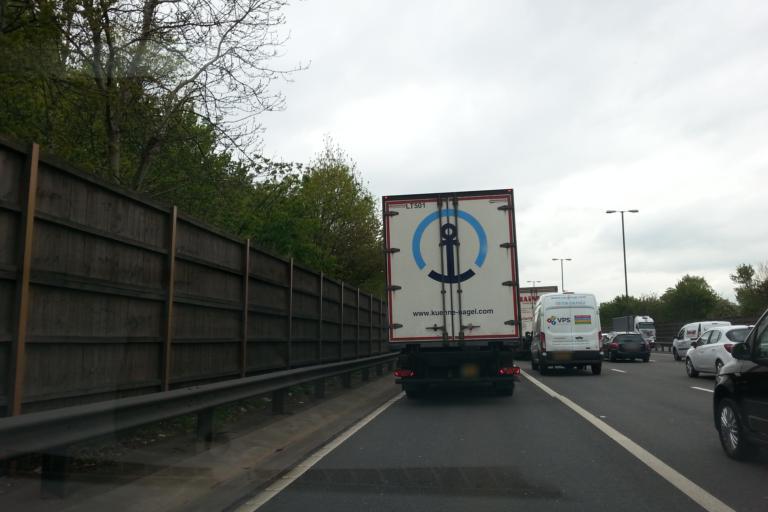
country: GB
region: England
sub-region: City and Borough of Birmingham
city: Hockley
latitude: 52.5448
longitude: -1.9164
